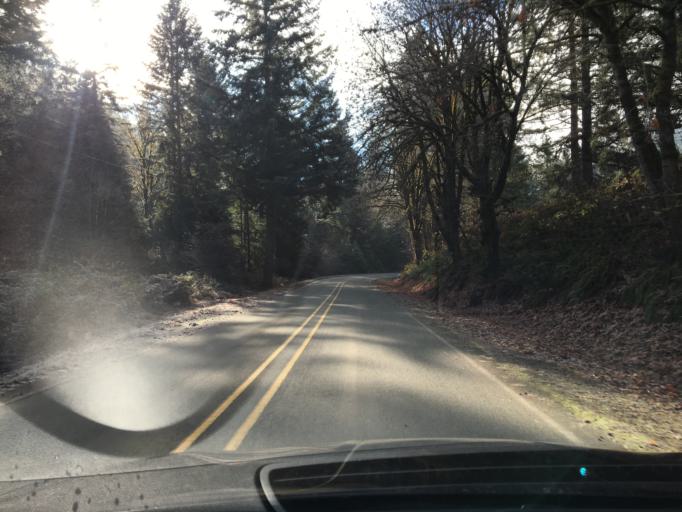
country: US
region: Oregon
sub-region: Douglas County
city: Roseburg
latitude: 43.3424
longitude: -123.5908
